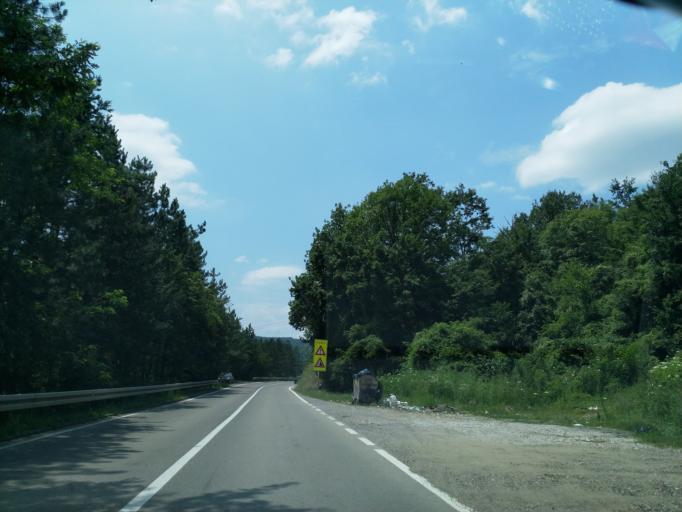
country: RS
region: Central Serbia
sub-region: Rasinski Okrug
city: Aleksandrovac
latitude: 43.4152
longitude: 21.1781
